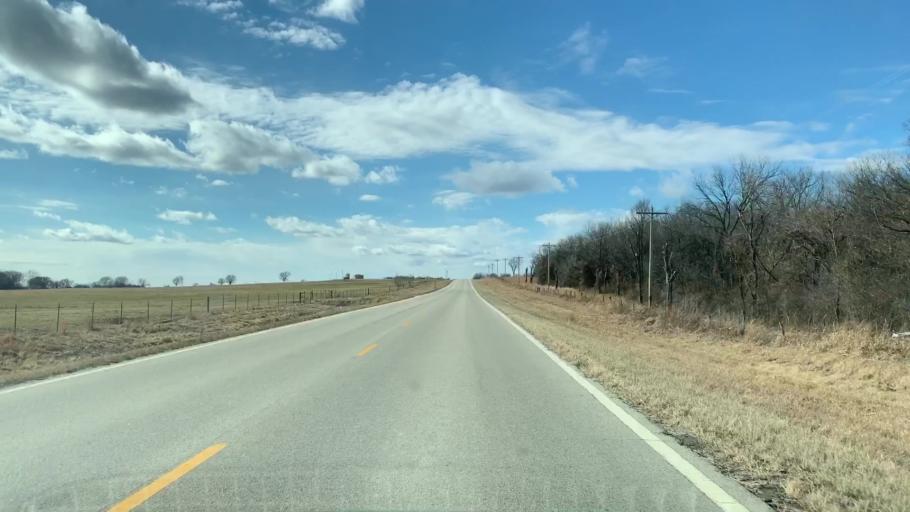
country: US
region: Kansas
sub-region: Neosho County
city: Chanute
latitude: 37.5289
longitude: -95.4280
